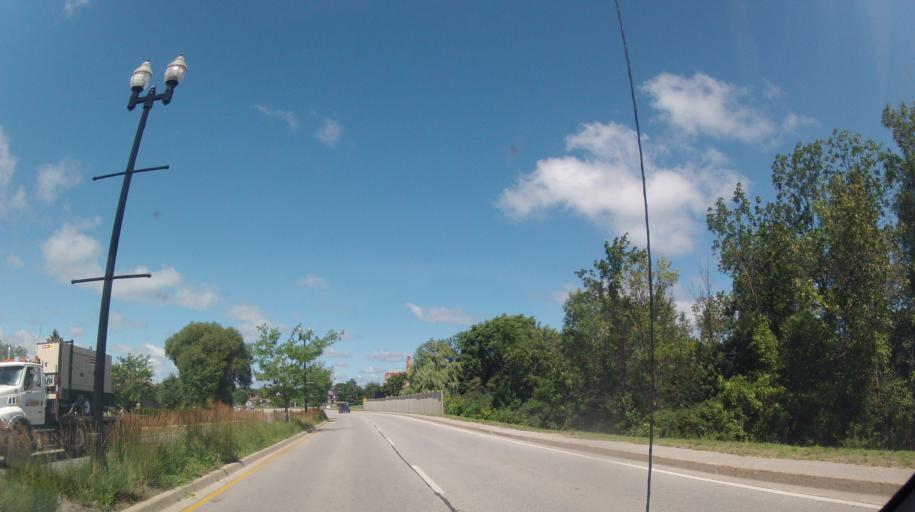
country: CA
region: Ontario
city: Collingwood
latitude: 44.5034
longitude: -80.1980
